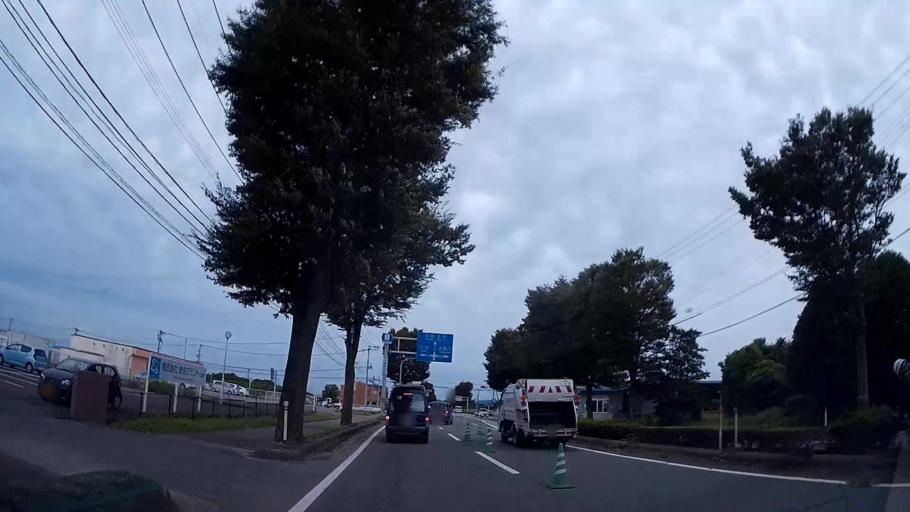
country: JP
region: Kumamoto
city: Ozu
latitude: 32.9106
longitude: 130.8447
